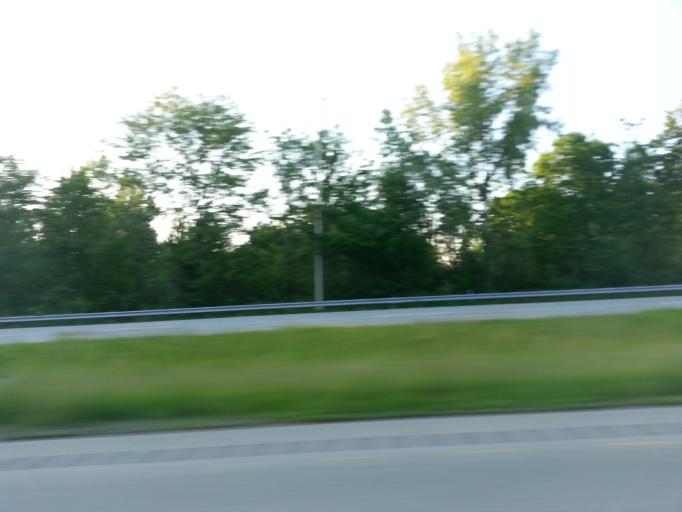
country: US
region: Indiana
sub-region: Fountain County
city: Covington
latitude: 40.1210
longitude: -87.4465
